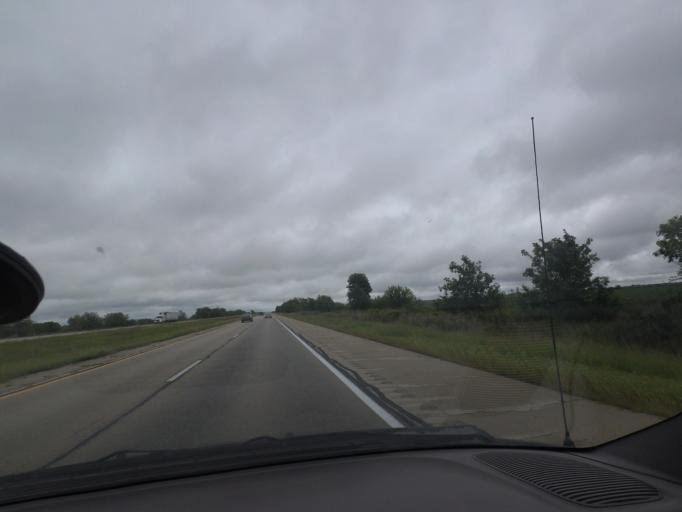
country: US
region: Illinois
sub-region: Piatt County
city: Cerro Gordo
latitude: 40.0190
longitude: -88.7162
